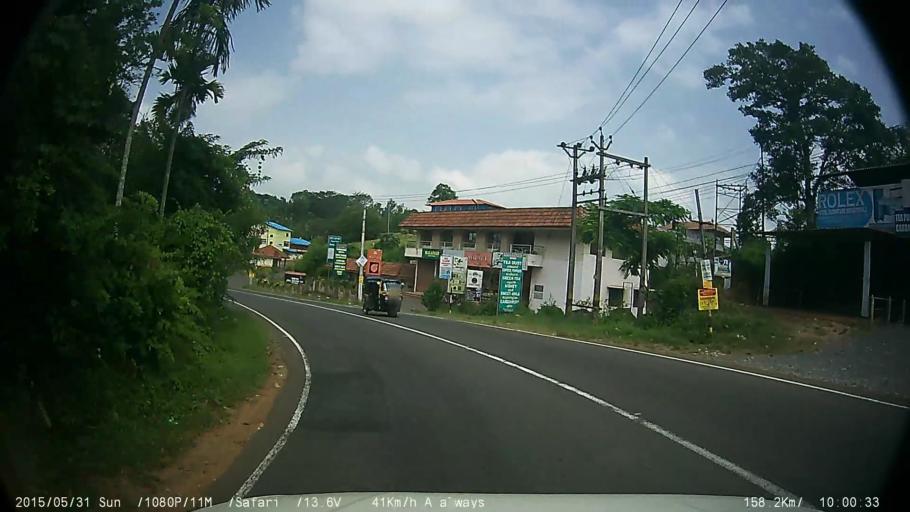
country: IN
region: Kerala
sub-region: Wayanad
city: Kalpetta
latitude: 11.5844
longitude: 76.0646
